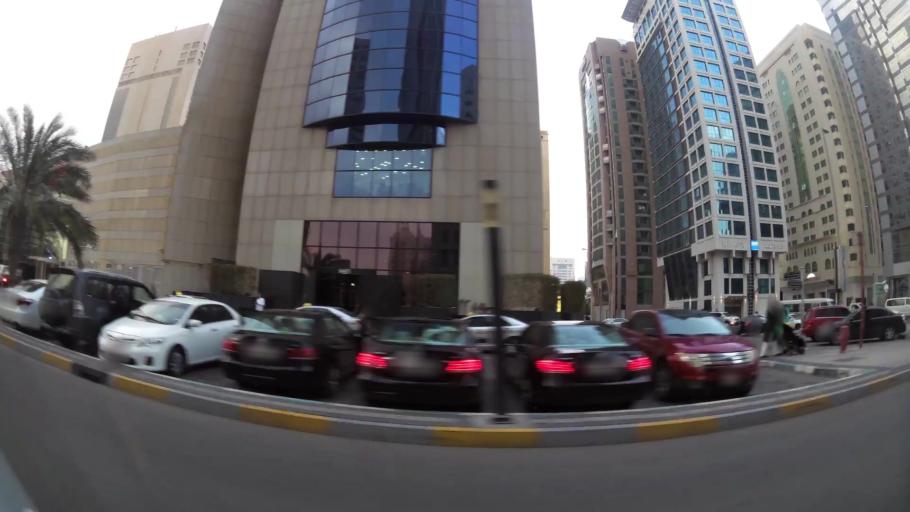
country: AE
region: Abu Dhabi
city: Abu Dhabi
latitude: 24.4959
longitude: 54.3655
